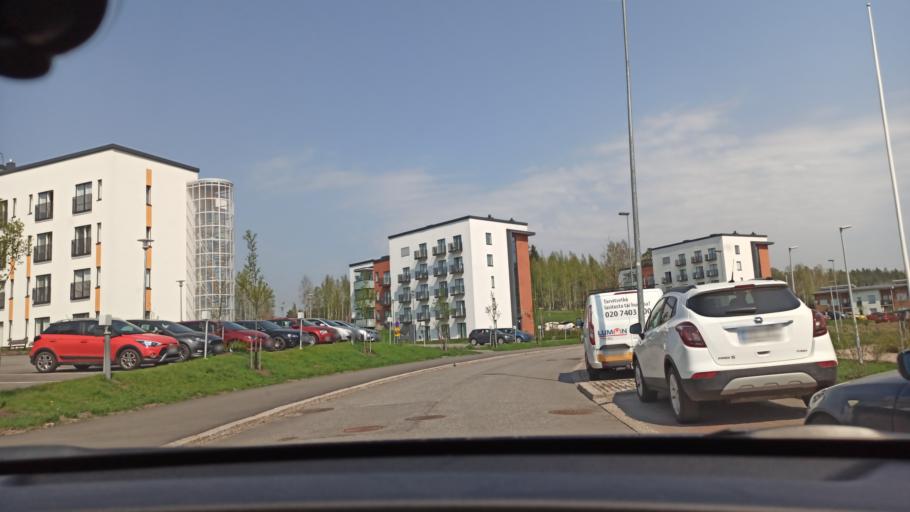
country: FI
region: Uusimaa
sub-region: Helsinki
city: Kirkkonummi
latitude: 60.1210
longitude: 24.4764
